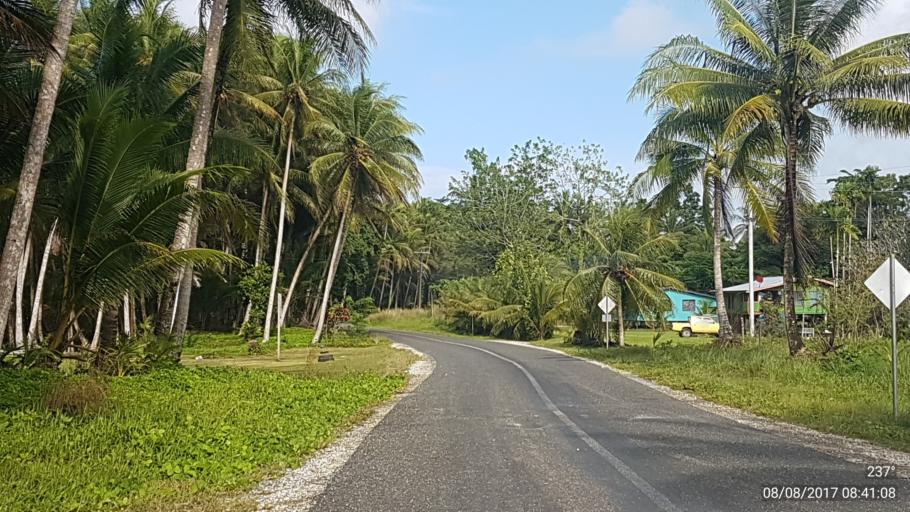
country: PG
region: Manus
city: Lorengau
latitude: -2.0792
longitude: 147.4084
